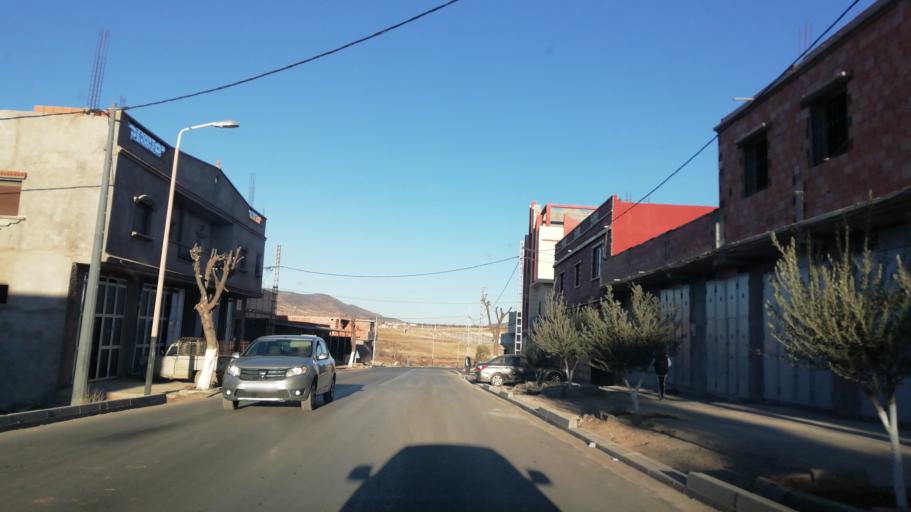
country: DZ
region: Tlemcen
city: Sebdou
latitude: 34.6541
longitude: -1.3154
